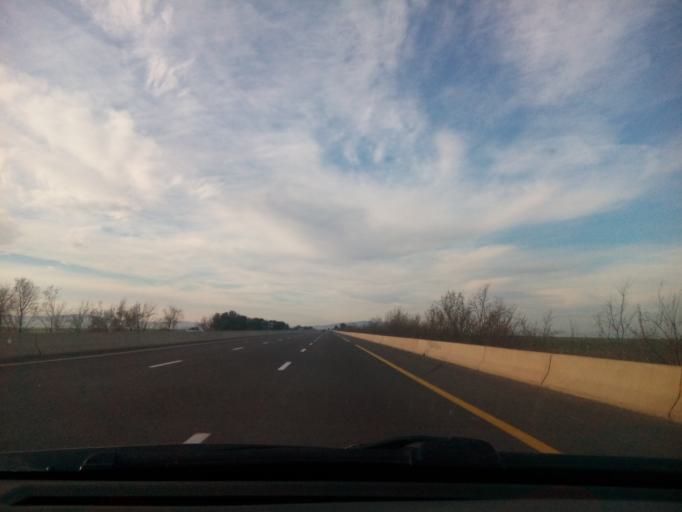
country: DZ
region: Mostaganem
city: Mostaganem
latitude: 35.6782
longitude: 0.1515
